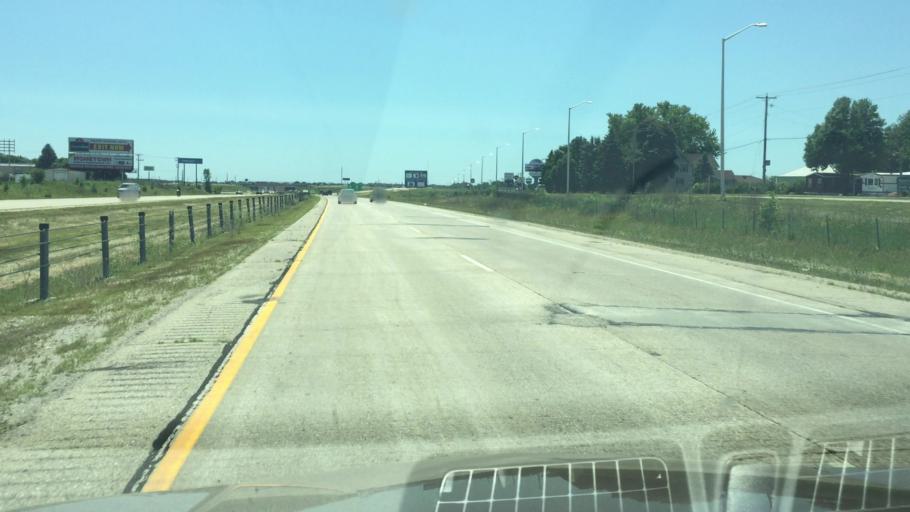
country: US
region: Wisconsin
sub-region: Dodge County
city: Beaver Dam
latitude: 43.4950
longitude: -88.8125
